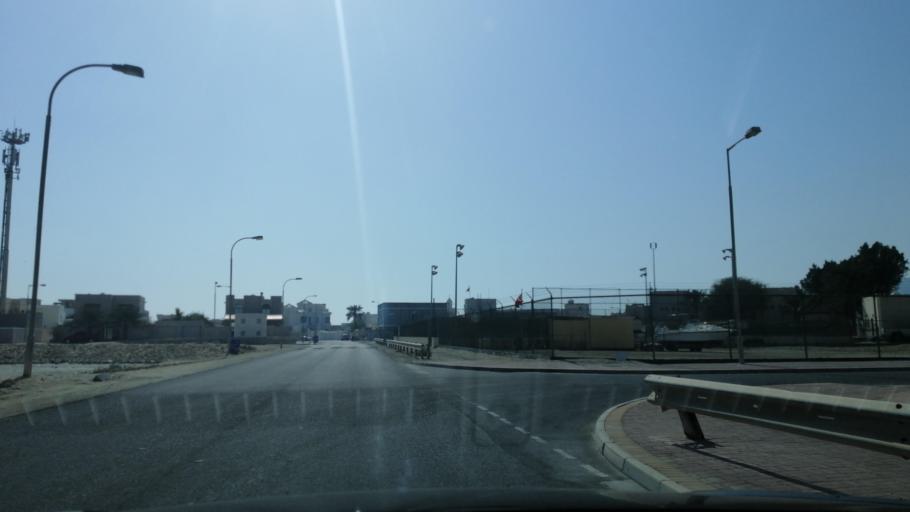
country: BH
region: Muharraq
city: Al Hadd
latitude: 26.2424
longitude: 50.6347
